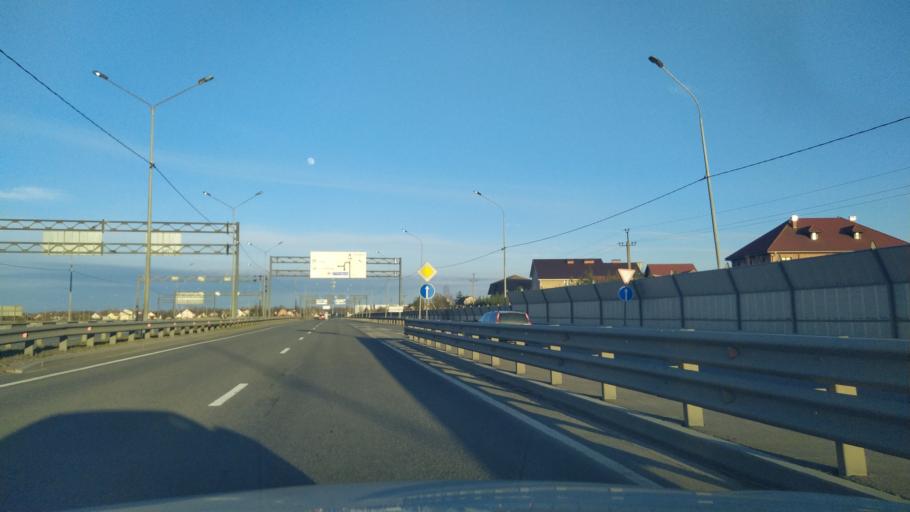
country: RU
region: St.-Petersburg
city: Aleksandrovskaya
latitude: 59.7422
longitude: 30.3162
